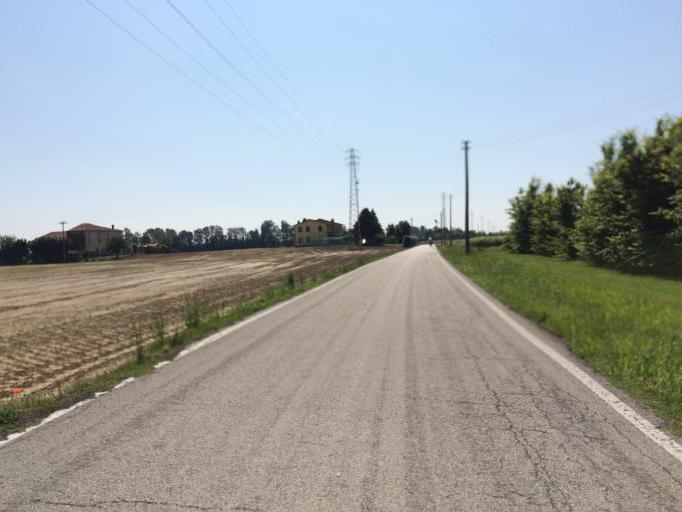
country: IT
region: Veneto
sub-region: Provincia di Vicenza
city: Montegalda
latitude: 45.4724
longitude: 11.6736
